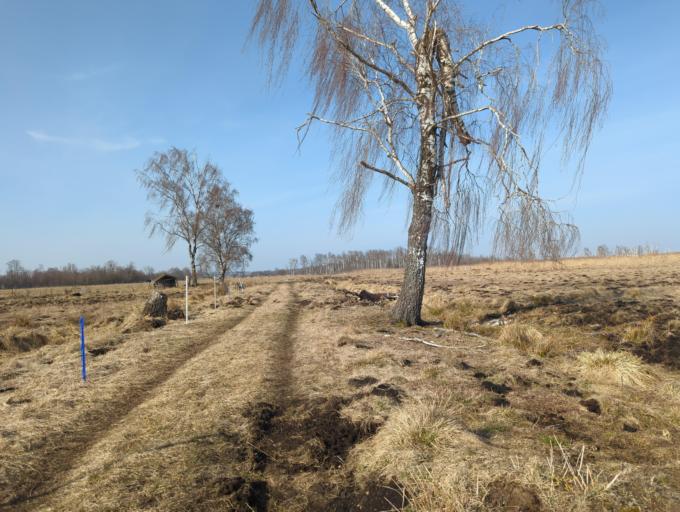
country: DE
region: Bavaria
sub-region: Swabia
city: Leipheim
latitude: 48.4840
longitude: 10.2142
